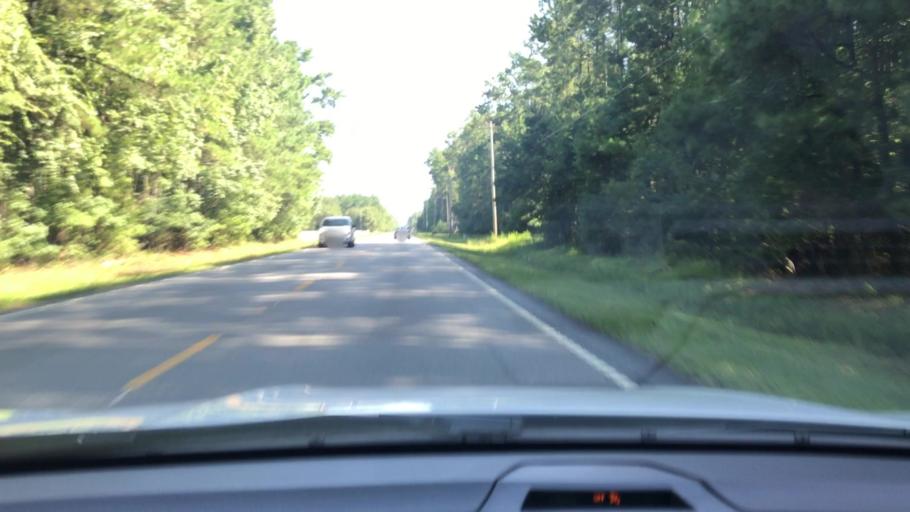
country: US
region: South Carolina
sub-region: Horry County
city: Conway
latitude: 33.7419
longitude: -79.0802
